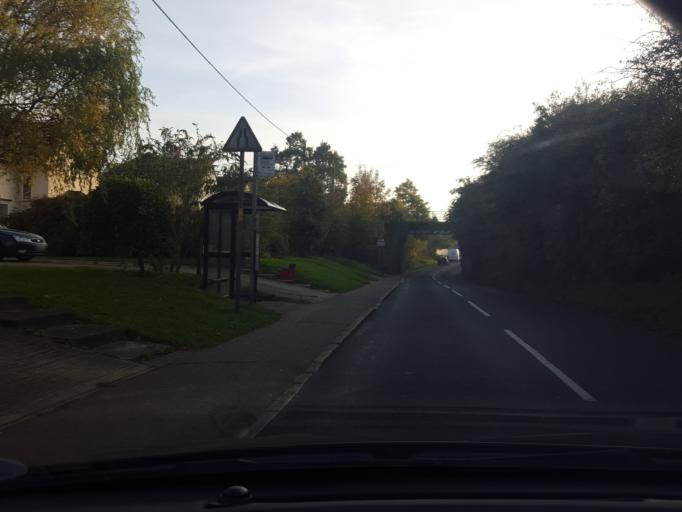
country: GB
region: England
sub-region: Essex
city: Frinton-on-Sea
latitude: 51.8414
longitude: 1.2188
